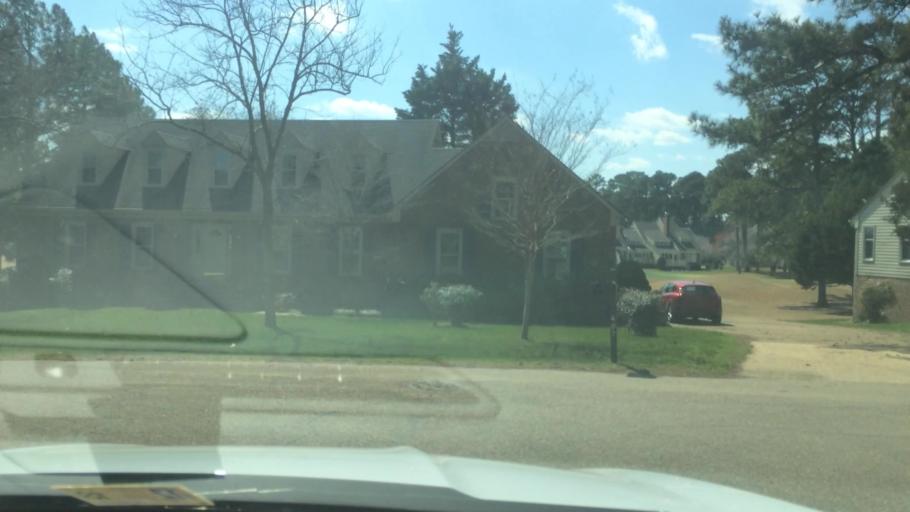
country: US
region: Virginia
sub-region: City of Williamsburg
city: Williamsburg
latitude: 37.2294
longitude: -76.6795
